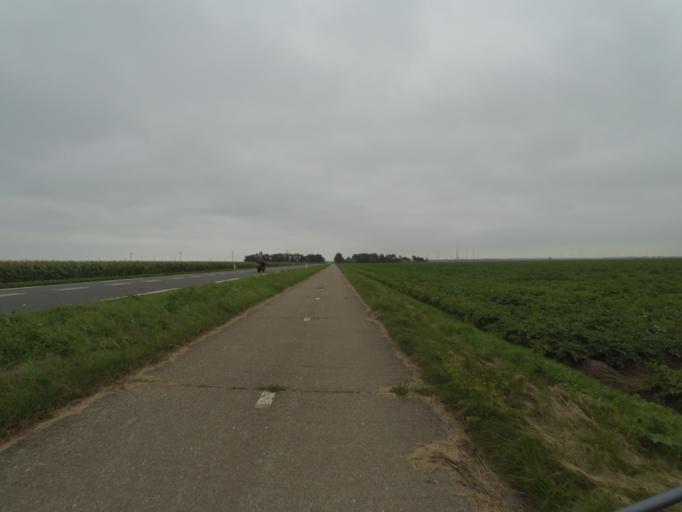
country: NL
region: Flevoland
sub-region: Gemeente Zeewolde
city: Zeewolde
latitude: 52.3813
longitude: 5.4487
